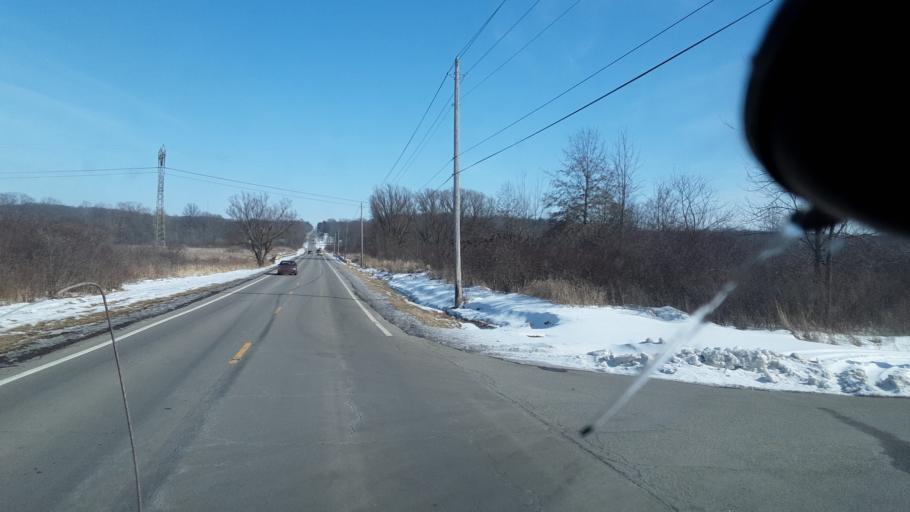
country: US
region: Ohio
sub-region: Columbiana County
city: Salem
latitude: 40.9441
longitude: -80.8339
